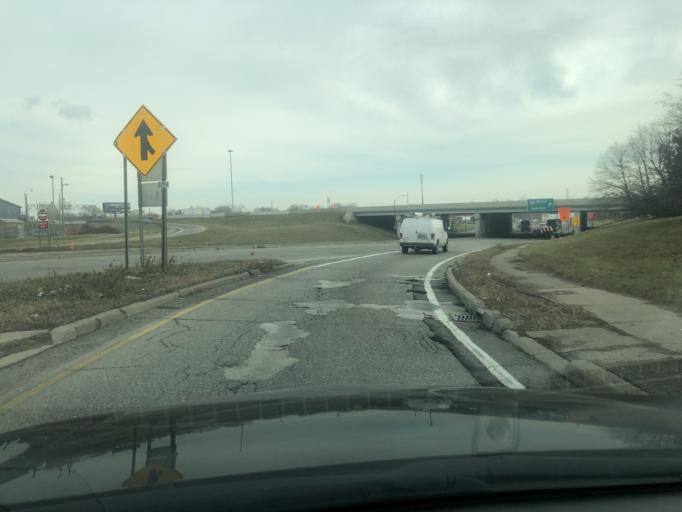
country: US
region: Michigan
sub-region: Wayne County
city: Melvindale
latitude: 42.2780
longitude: -83.1576
